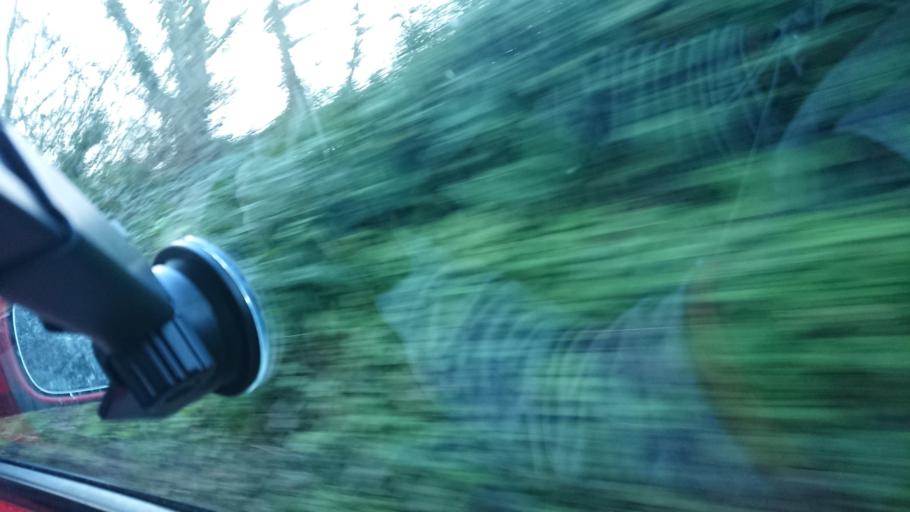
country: GB
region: England
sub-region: Cornwall
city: Looe
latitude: 50.3449
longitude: -4.4770
